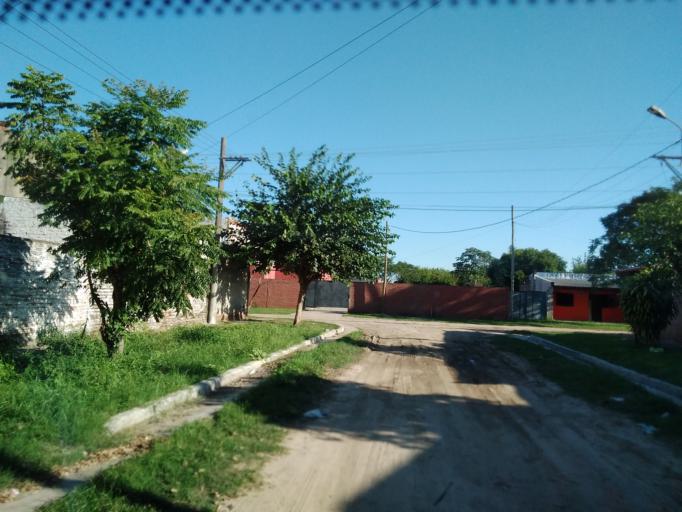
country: AR
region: Corrientes
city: Corrientes
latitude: -27.5074
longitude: -58.7809
